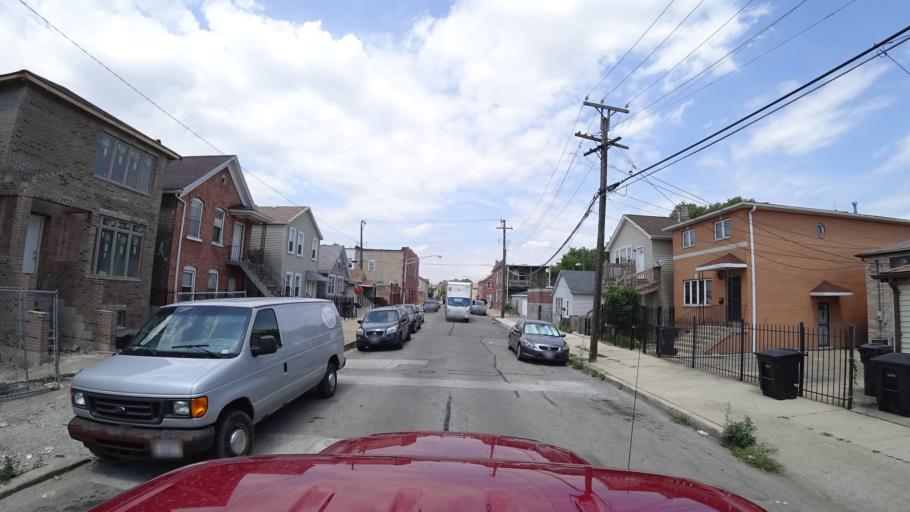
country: US
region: Illinois
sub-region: Cook County
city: Chicago
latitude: 41.8401
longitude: -87.6532
